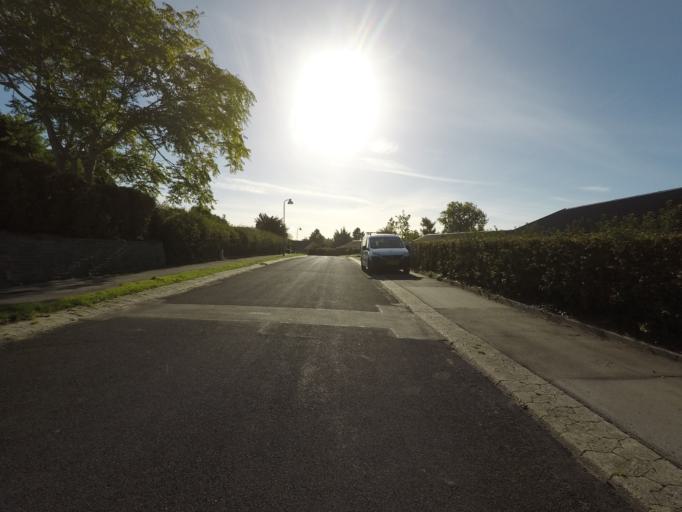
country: DK
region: Capital Region
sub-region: Egedal Kommune
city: Smorumnedre
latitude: 55.7367
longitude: 12.3013
